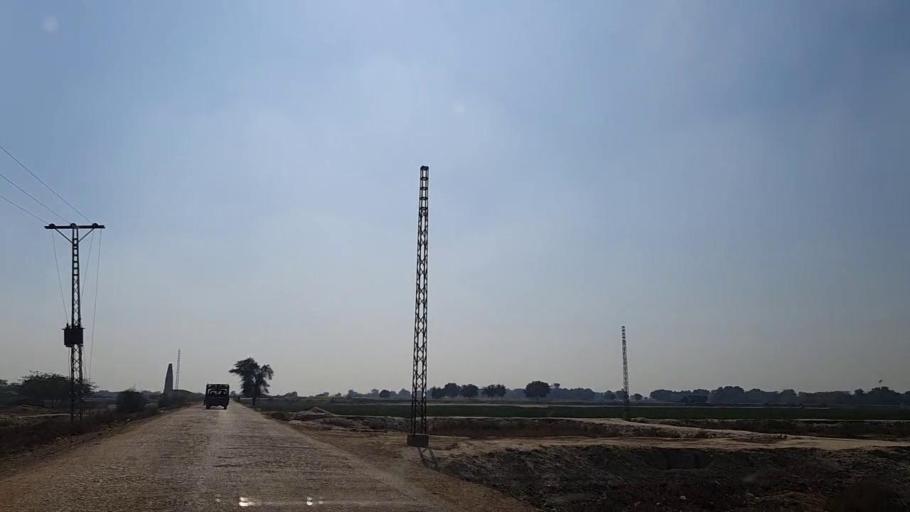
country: PK
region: Sindh
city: Sakrand
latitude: 26.2932
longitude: 68.1081
